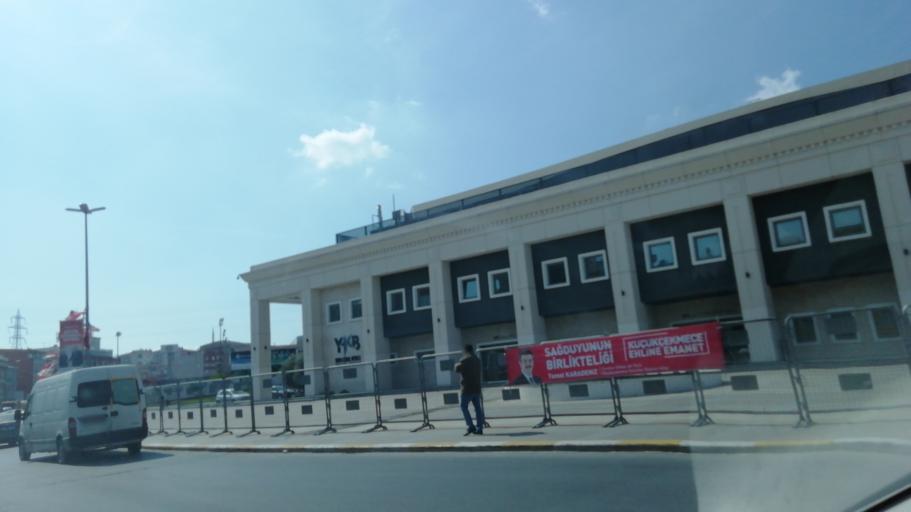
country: TR
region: Istanbul
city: Mahmutbey
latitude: 41.0303
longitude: 28.8041
